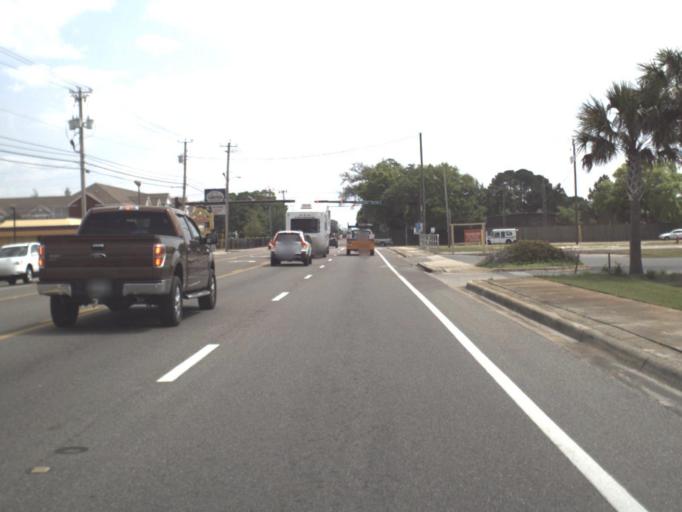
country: US
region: Florida
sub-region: Escambia County
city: Warrington
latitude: 30.3884
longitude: -87.2741
